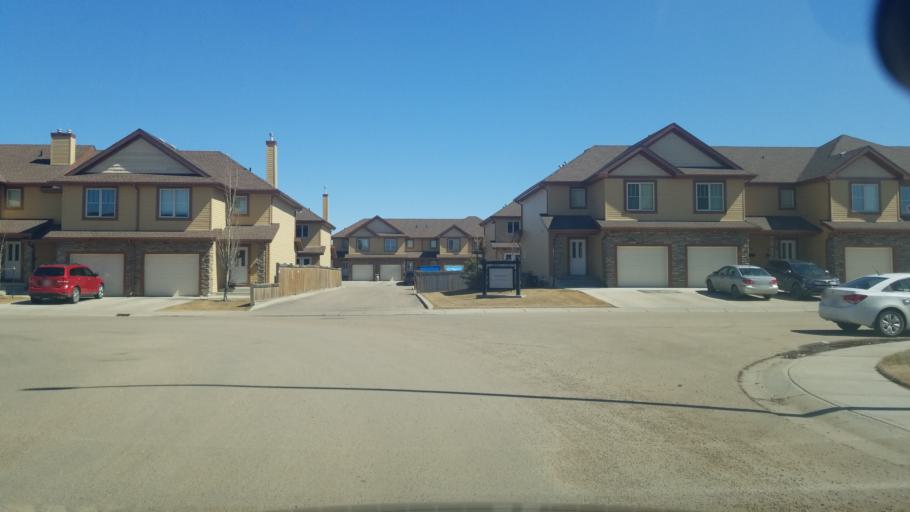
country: CA
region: Saskatchewan
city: Lloydminster
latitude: 53.2506
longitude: -110.0166
